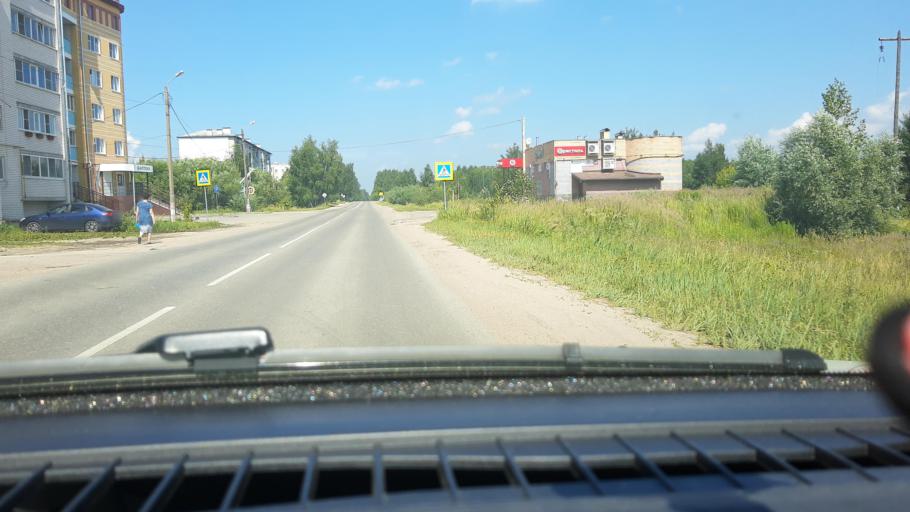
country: RU
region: Nizjnij Novgorod
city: Afonino
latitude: 56.3029
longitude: 44.1844
